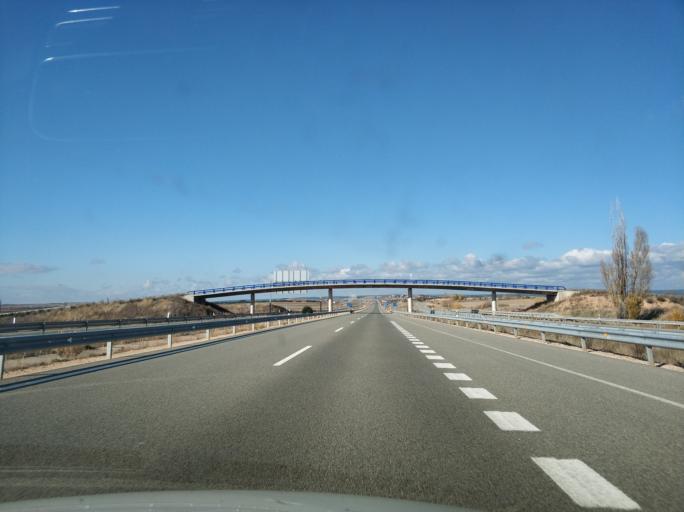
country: ES
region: Castille and Leon
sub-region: Provincia de Soria
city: Frechilla de Almazan
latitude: 41.4504
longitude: -2.5099
